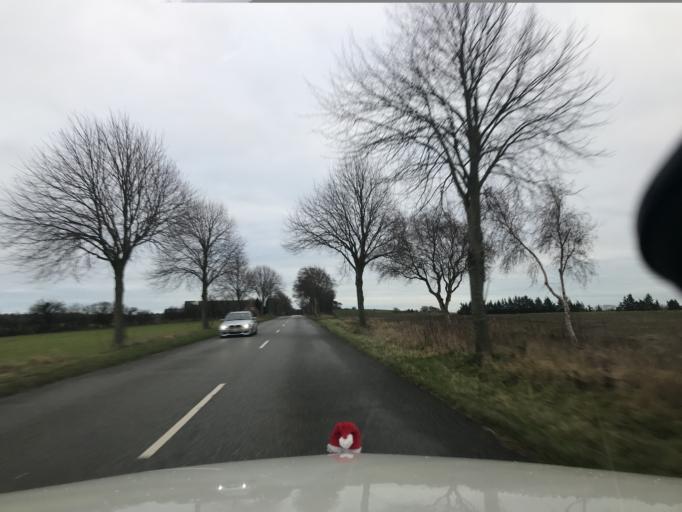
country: DK
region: South Denmark
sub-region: Sonderborg Kommune
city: Broager
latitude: 54.8865
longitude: 9.6895
